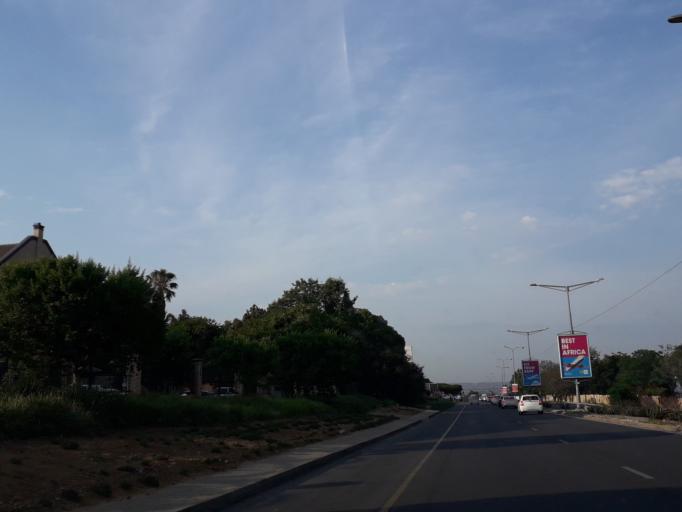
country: ZA
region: Gauteng
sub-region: City of Johannesburg Metropolitan Municipality
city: Diepsloot
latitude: -26.0495
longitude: 28.0243
